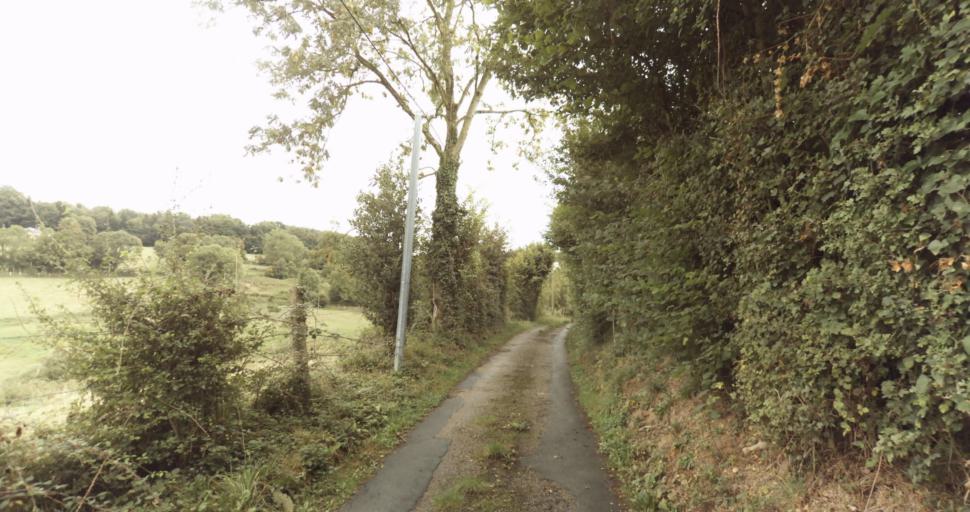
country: FR
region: Lower Normandy
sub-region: Departement de l'Orne
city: Vimoutiers
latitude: 48.8635
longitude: 0.1738
